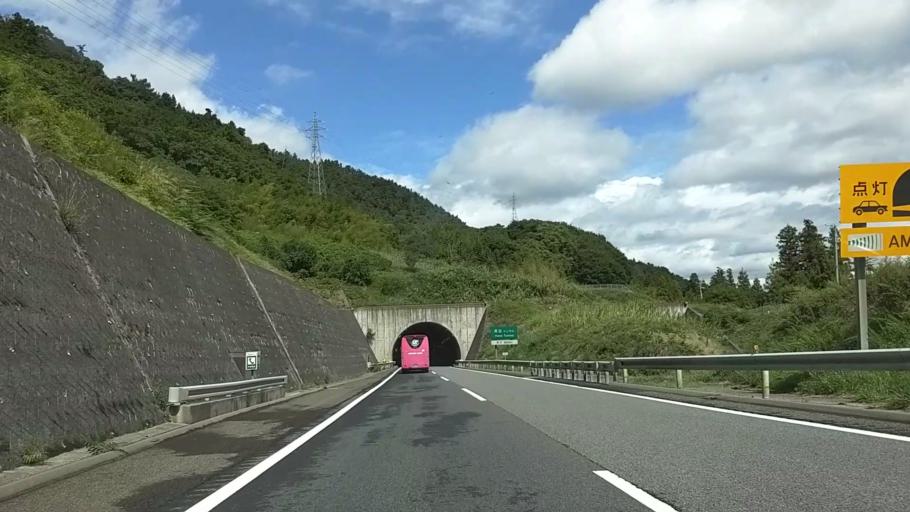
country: JP
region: Nagano
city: Nagano-shi
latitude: 36.5437
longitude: 138.0977
